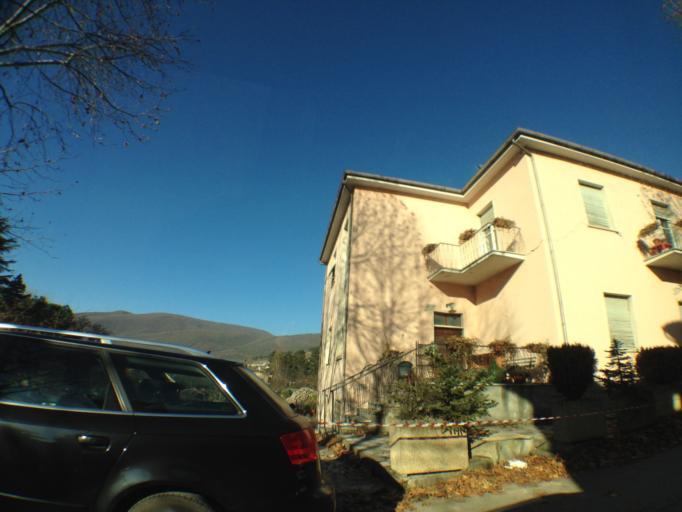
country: IT
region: Umbria
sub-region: Provincia di Perugia
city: Norcia
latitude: 42.7959
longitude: 13.0927
